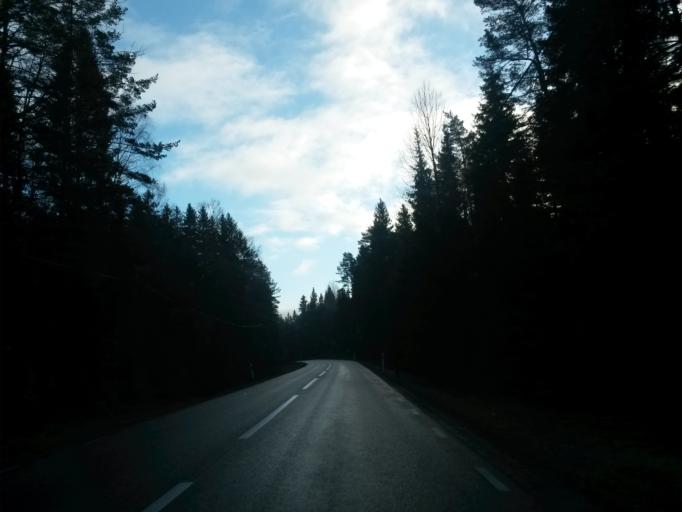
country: SE
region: Vaestra Goetaland
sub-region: Boras Kommun
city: Boras
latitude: 57.8499
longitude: 12.9490
